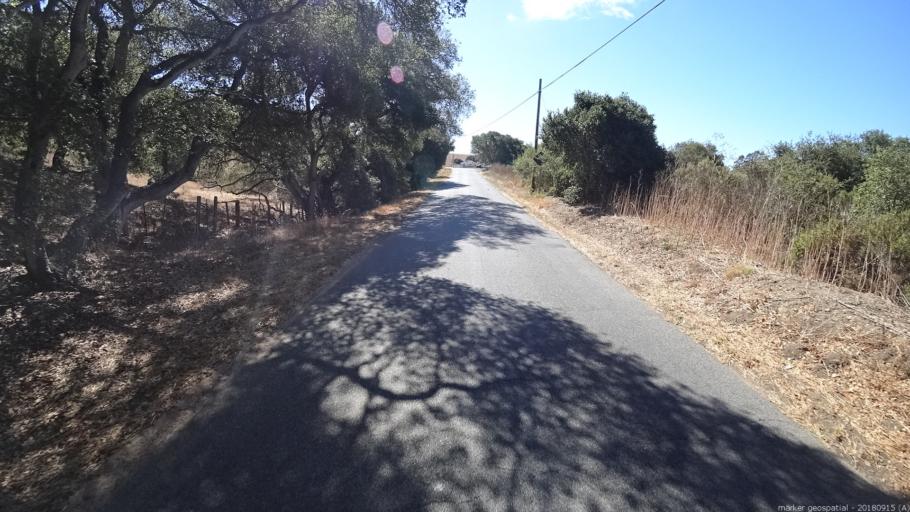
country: US
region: California
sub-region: Monterey County
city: Las Lomas
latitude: 36.8768
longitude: -121.7451
